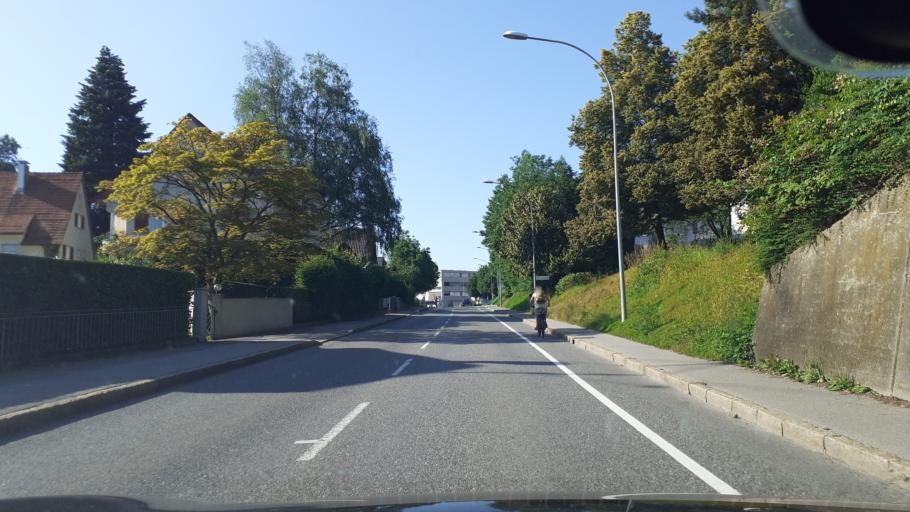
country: AT
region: Vorarlberg
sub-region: Politischer Bezirk Bregenz
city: Lauterach
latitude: 47.4911
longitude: 9.7419
